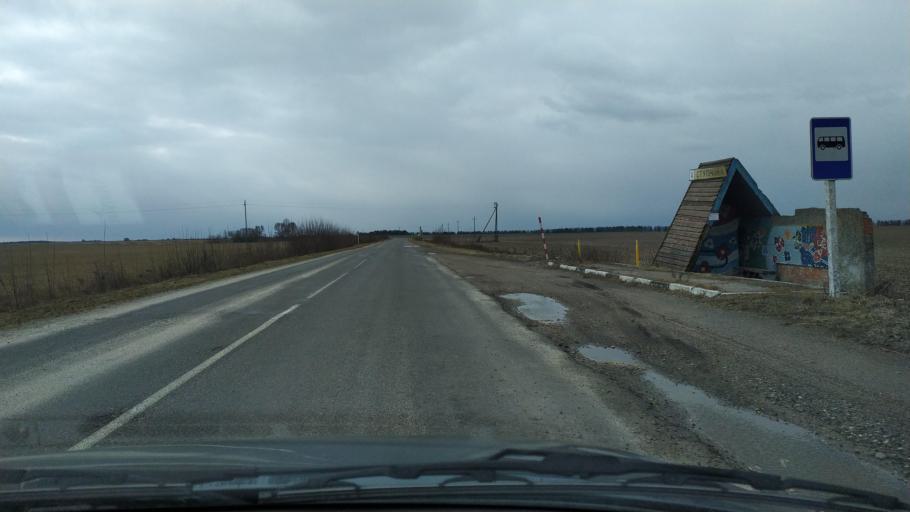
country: BY
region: Brest
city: Kamyanyets
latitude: 52.4278
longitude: 23.8155
